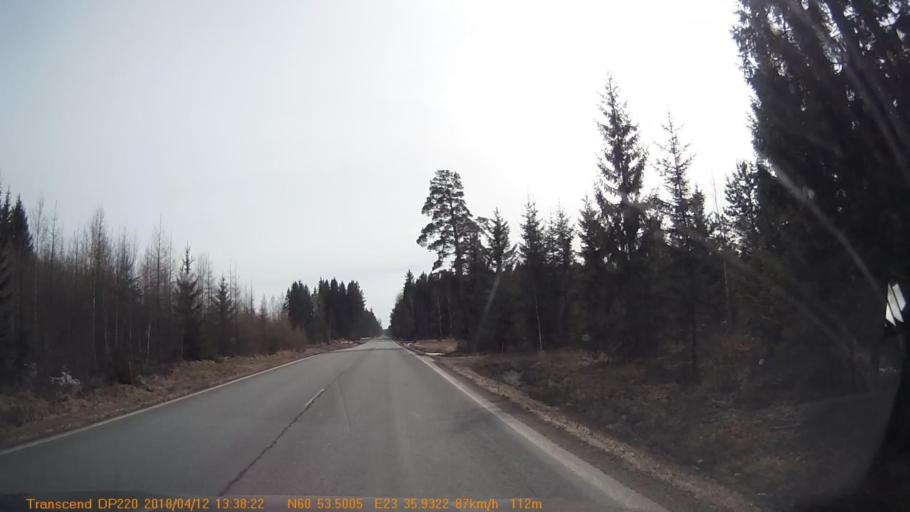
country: FI
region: Haeme
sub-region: Forssa
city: Forssa
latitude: 60.8913
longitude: 23.5990
